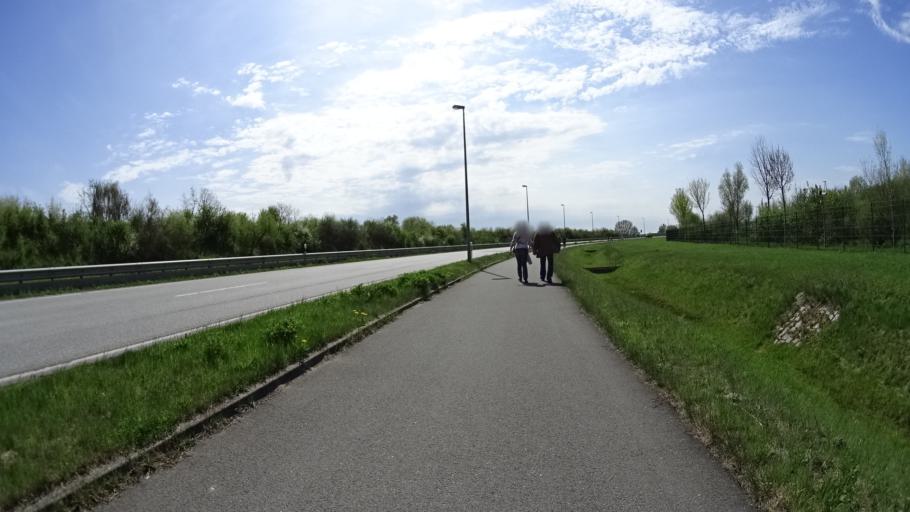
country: DE
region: Lower Saxony
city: Neu Wulmstorf
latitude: 53.5313
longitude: 9.8434
